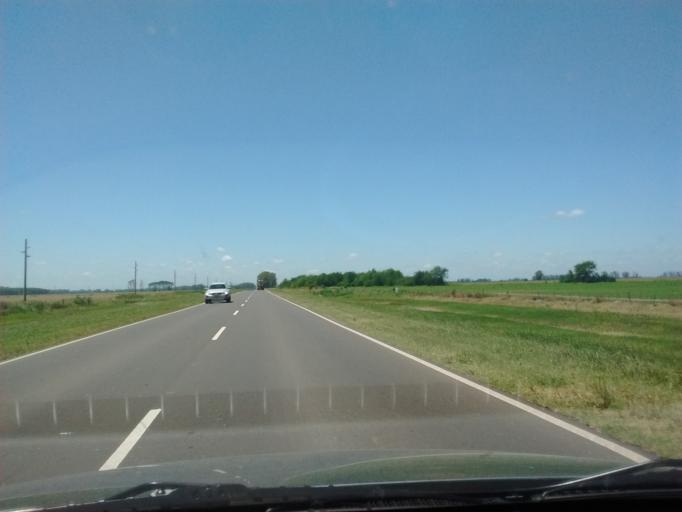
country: AR
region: Entre Rios
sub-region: Departamento de Gualeguay
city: Gualeguay
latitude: -33.0831
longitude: -59.3913
